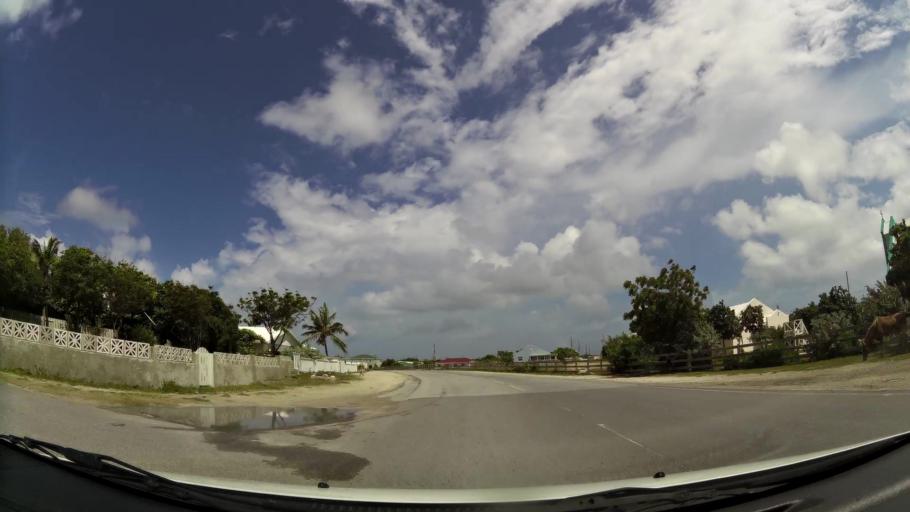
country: TC
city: Cockburn Town
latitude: 21.4542
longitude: -71.1447
